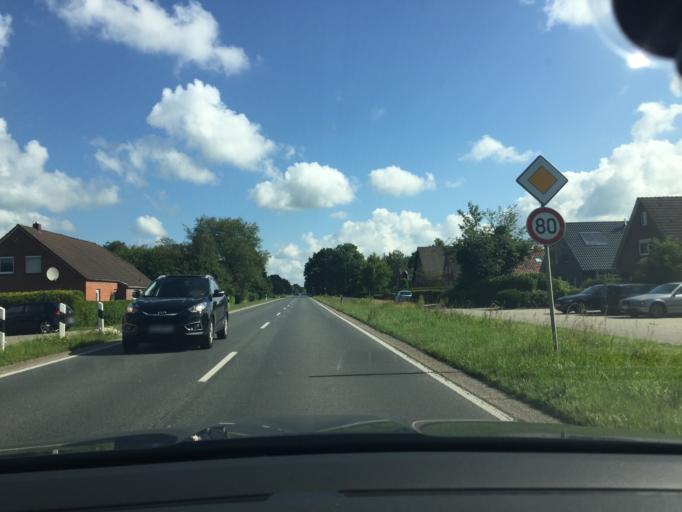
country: DE
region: Lower Saxony
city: Aurich
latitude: 53.4987
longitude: 7.5071
